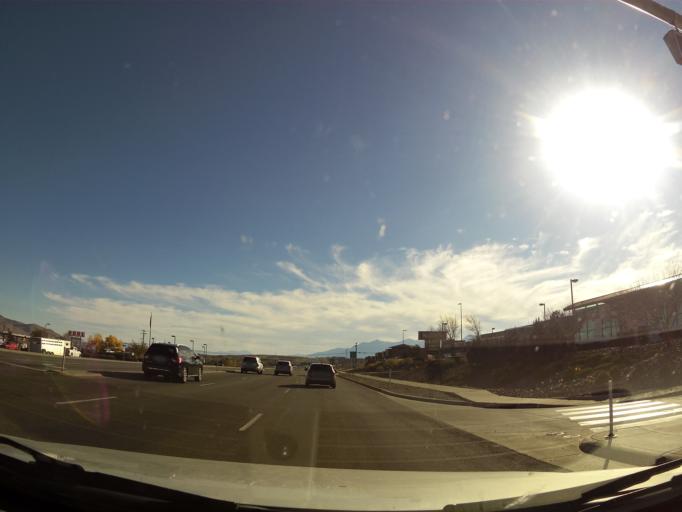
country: US
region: Nevada
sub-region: Carson City
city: Carson City
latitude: 39.1284
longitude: -119.7708
